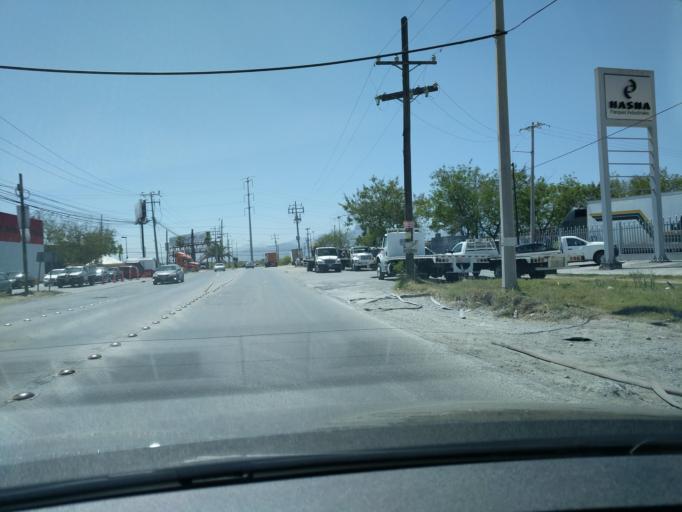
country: MX
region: Nuevo Leon
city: Apodaca
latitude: 25.7865
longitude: -100.1594
